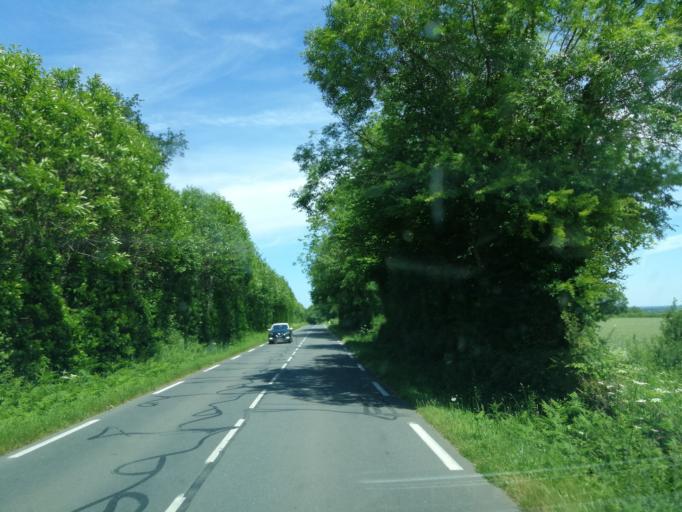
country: FR
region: Pays de la Loire
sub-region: Departement de la Vendee
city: Saint-Pierre-du-Chemin
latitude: 46.7007
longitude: -0.6905
